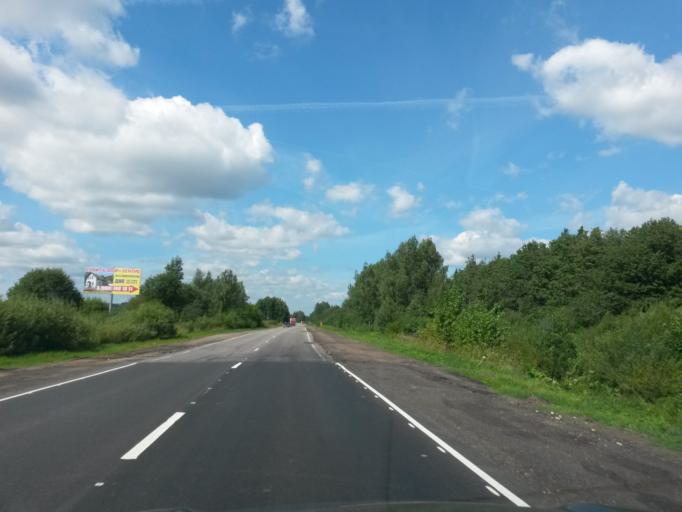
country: RU
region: Jaroslavl
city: Yaroslavl
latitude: 57.5298
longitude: 39.8763
